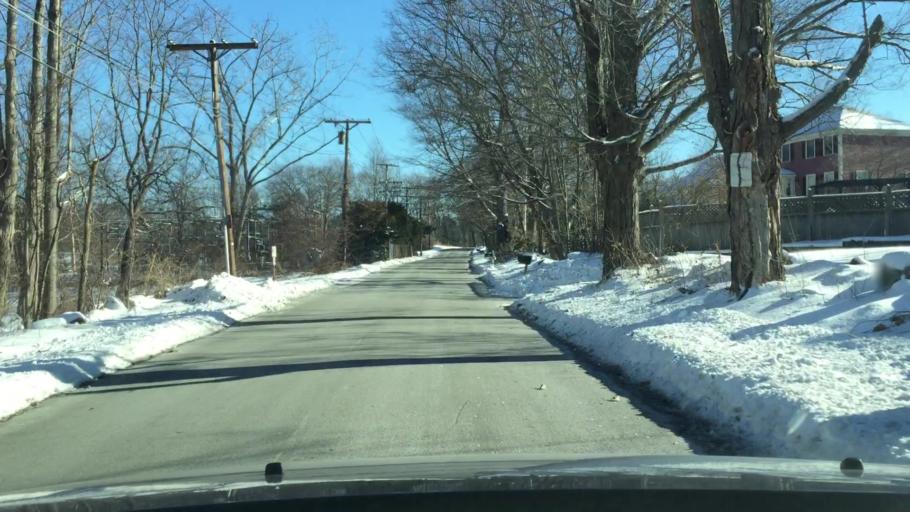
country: US
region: Massachusetts
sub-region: Essex County
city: North Andover
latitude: 42.6889
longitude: -71.1069
